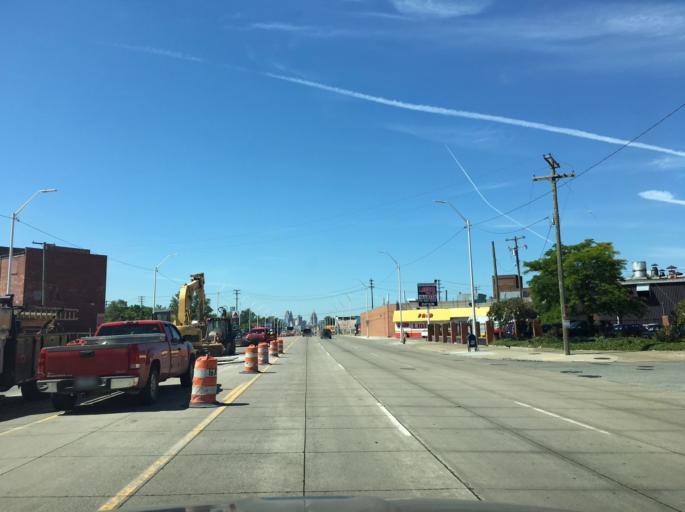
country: US
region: Michigan
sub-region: Wayne County
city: Hamtramck
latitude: 42.3689
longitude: -83.0213
